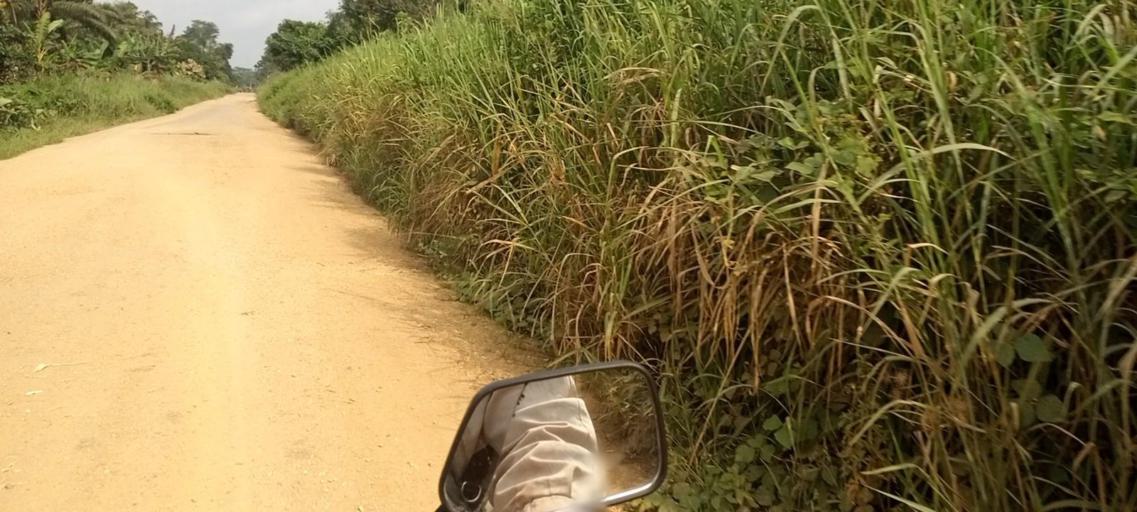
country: CD
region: Eastern Province
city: Kisangani
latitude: 0.2902
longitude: 25.4695
